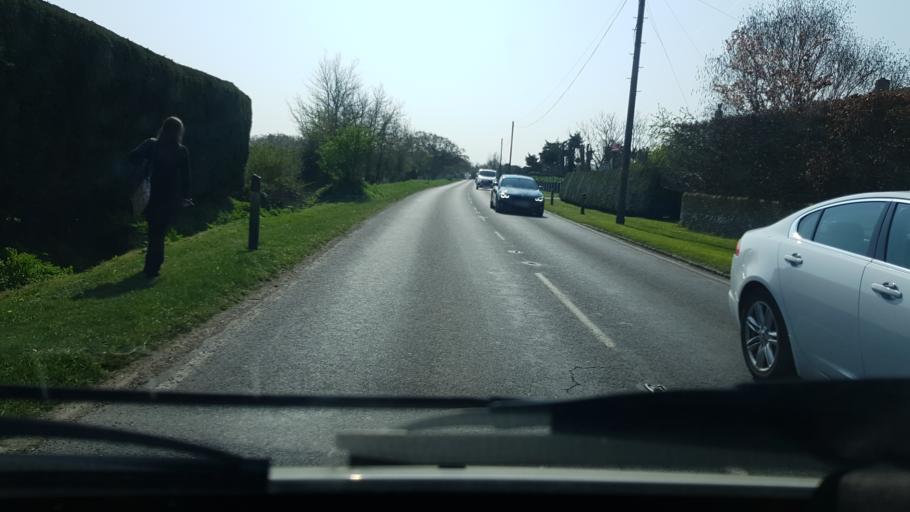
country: GB
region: England
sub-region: West Sussex
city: Chichester
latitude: 50.8139
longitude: -0.8033
